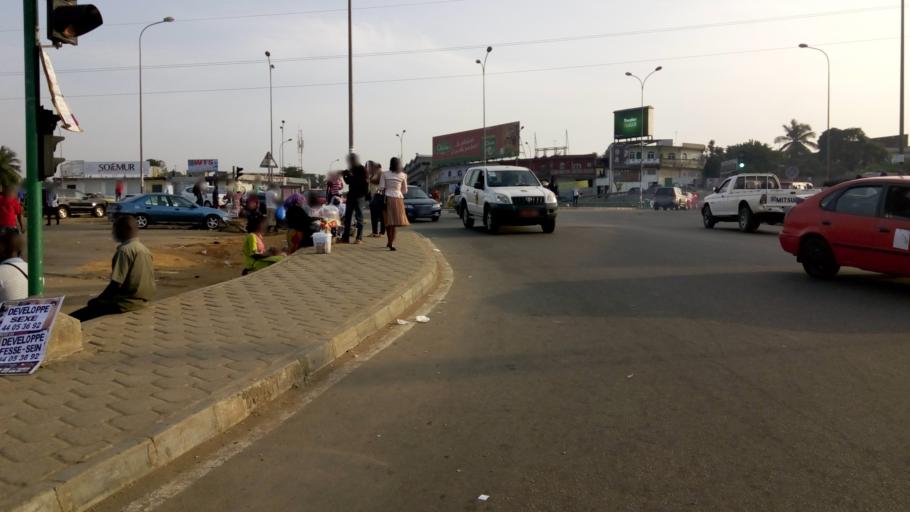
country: CI
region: Lagunes
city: Abidjan
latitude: 5.3530
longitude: -3.9770
